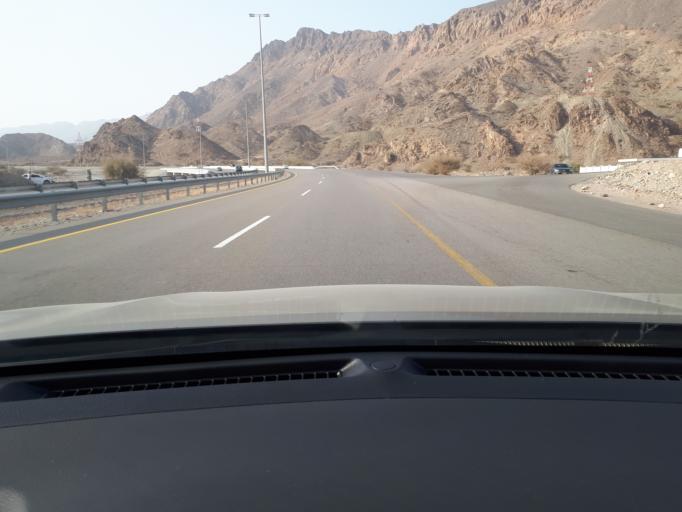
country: OM
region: Muhafazat Masqat
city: Muscat
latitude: 23.2710
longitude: 58.7565
